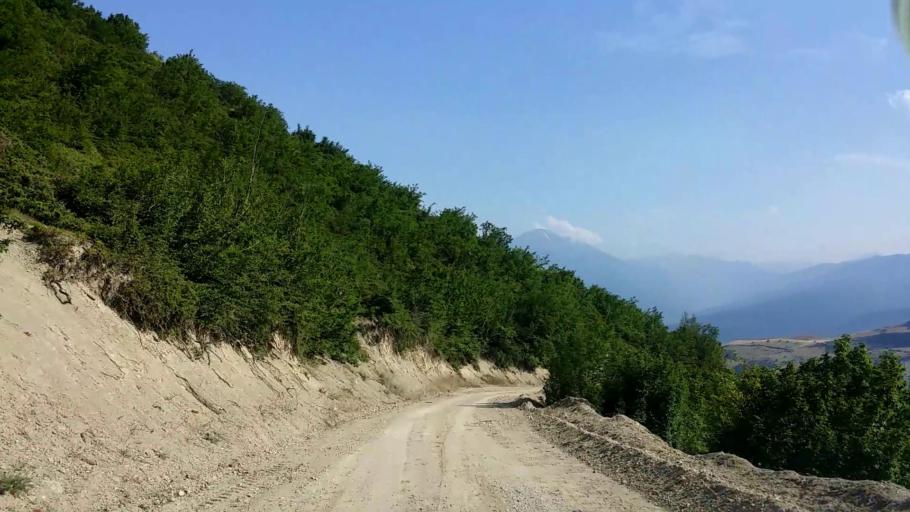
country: IR
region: Mazandaran
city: Chalus
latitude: 36.5524
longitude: 51.2949
